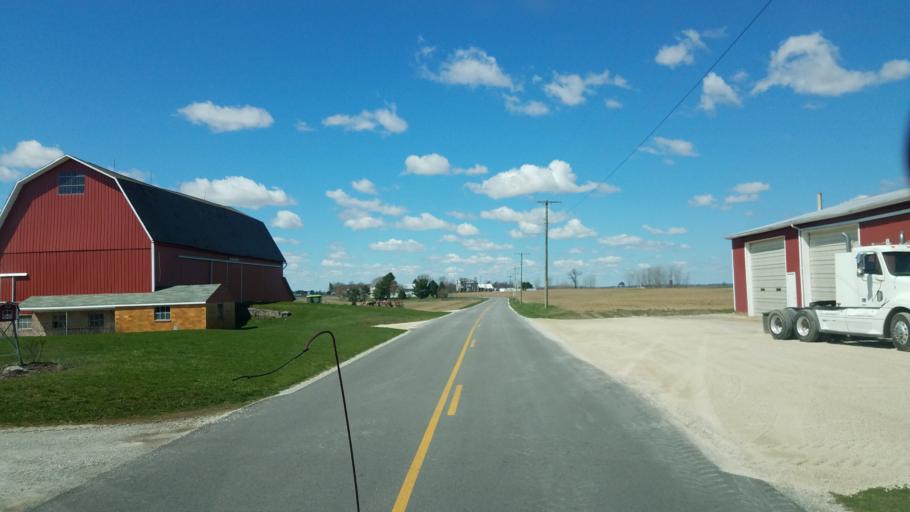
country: US
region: Ohio
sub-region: Seneca County
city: Fostoria
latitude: 41.1568
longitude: -83.4586
